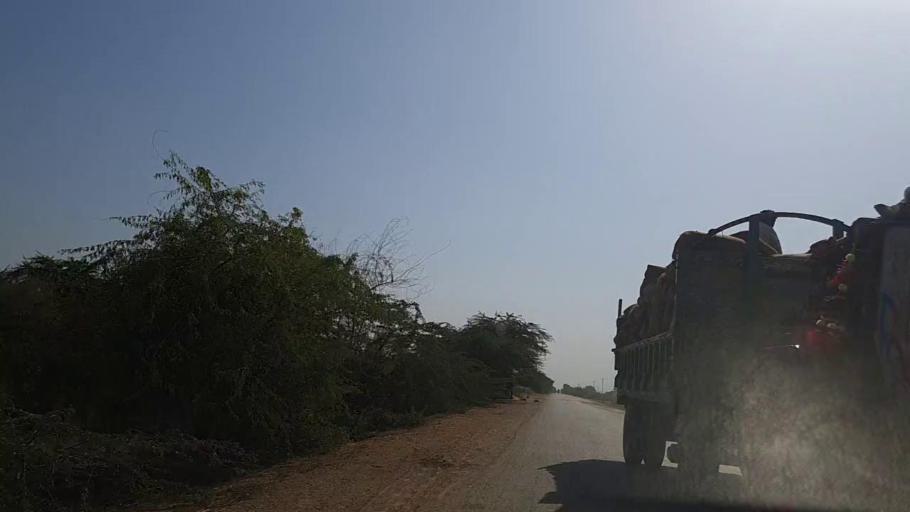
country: PK
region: Sindh
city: Mirpur Batoro
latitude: 24.6027
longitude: 68.2949
